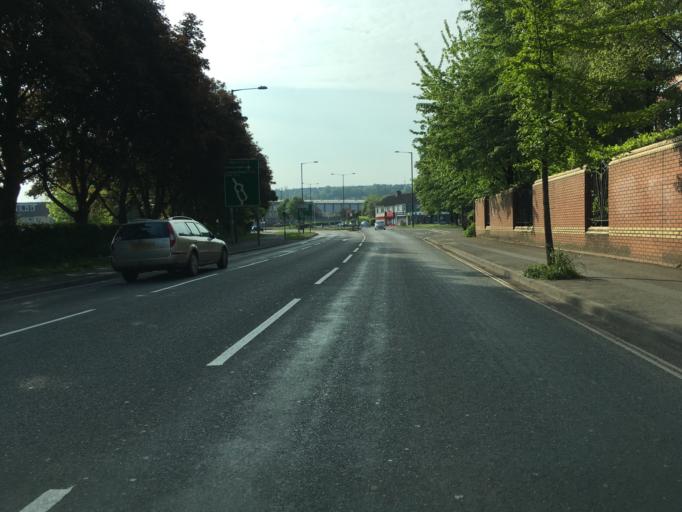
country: GB
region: England
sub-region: Bristol
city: Bristol
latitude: 51.4359
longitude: -2.6199
